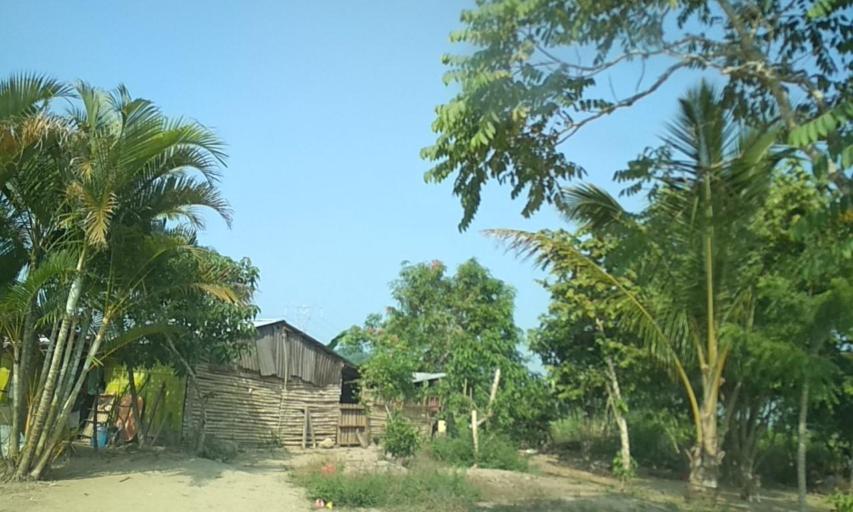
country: MX
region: Veracruz
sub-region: Atzalan
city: Colonias Pedernales
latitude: 20.0507
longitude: -96.9930
